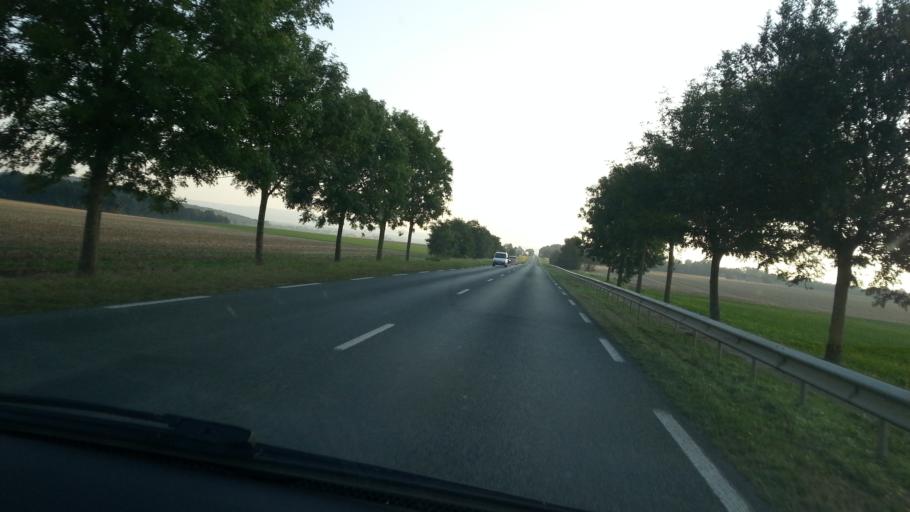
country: FR
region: Picardie
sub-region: Departement de l'Oise
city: Grandfresnoy
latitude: 49.3933
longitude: 2.6231
